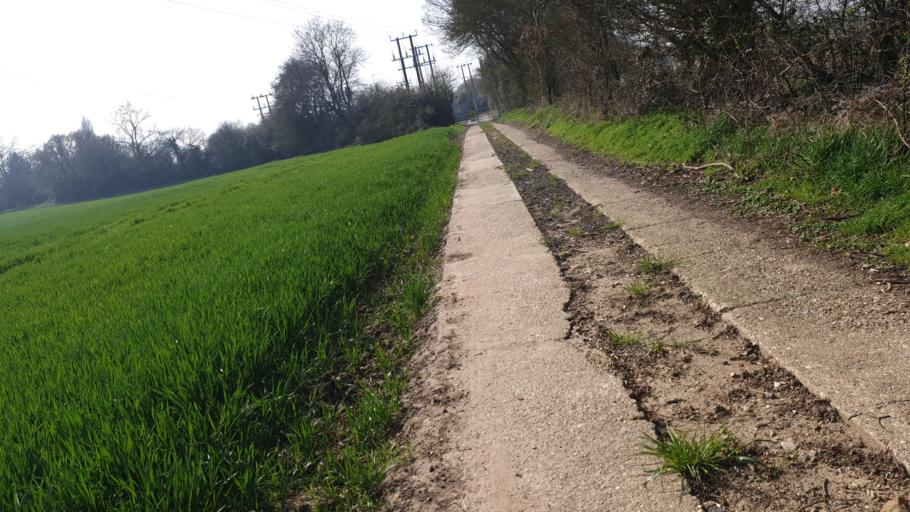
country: GB
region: England
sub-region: Essex
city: Mistley
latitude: 51.9197
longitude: 1.1464
